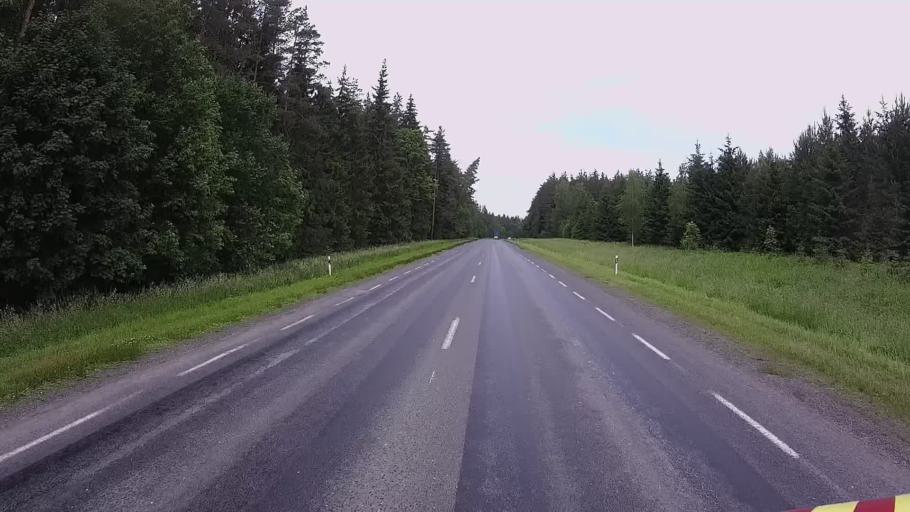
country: EE
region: Viljandimaa
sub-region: Viljandi linn
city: Viljandi
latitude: 58.2948
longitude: 25.5778
